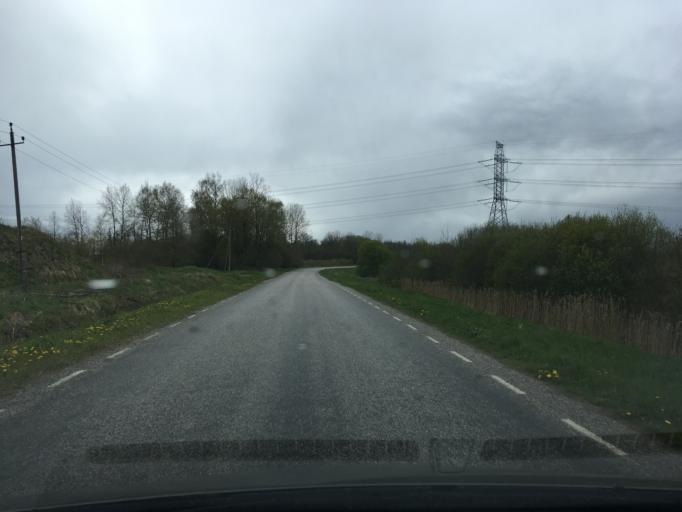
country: EE
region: Harju
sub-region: Rae vald
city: Vaida
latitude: 59.3047
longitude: 24.9882
